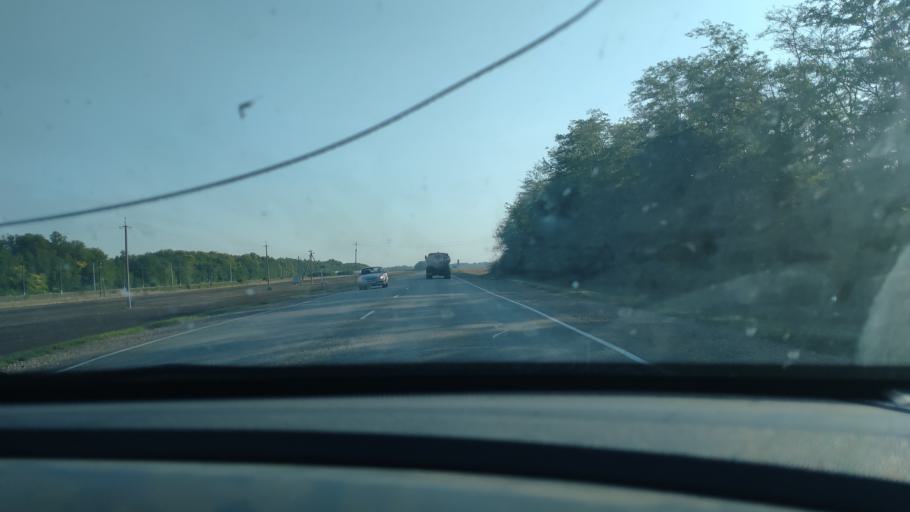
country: RU
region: Krasnodarskiy
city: Starominskaya
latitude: 46.4799
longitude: 39.0508
